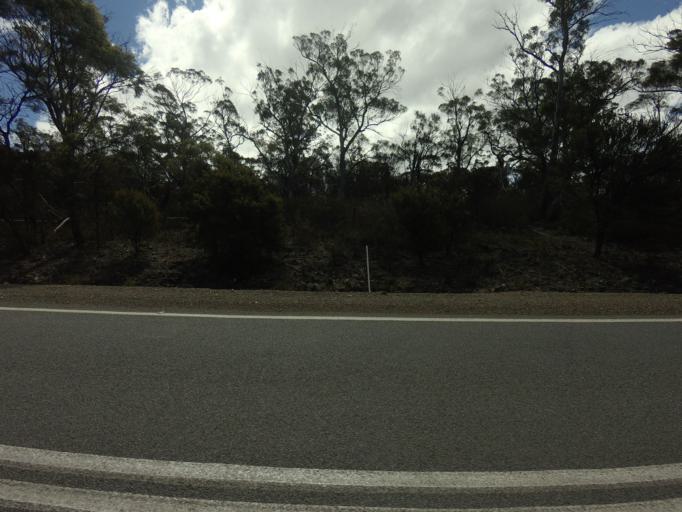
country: AU
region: Tasmania
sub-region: Break O'Day
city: St Helens
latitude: -42.0147
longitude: 147.9771
